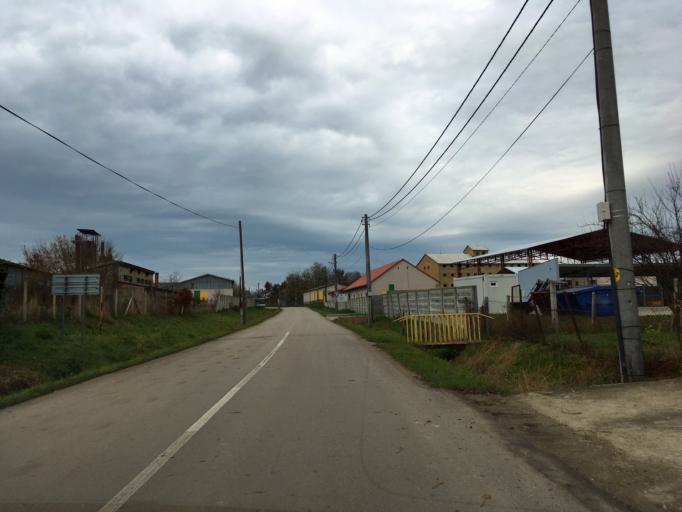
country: SK
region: Nitriansky
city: Svodin
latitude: 48.0169
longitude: 18.4105
